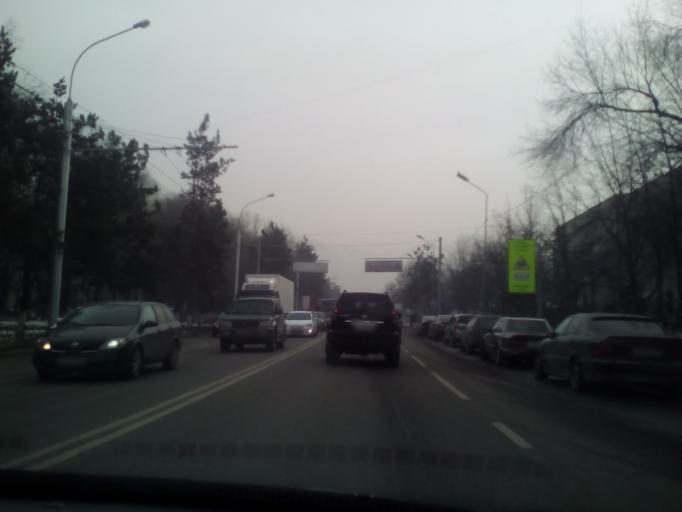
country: KZ
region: Almaty Qalasy
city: Almaty
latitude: 43.2382
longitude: 76.8299
